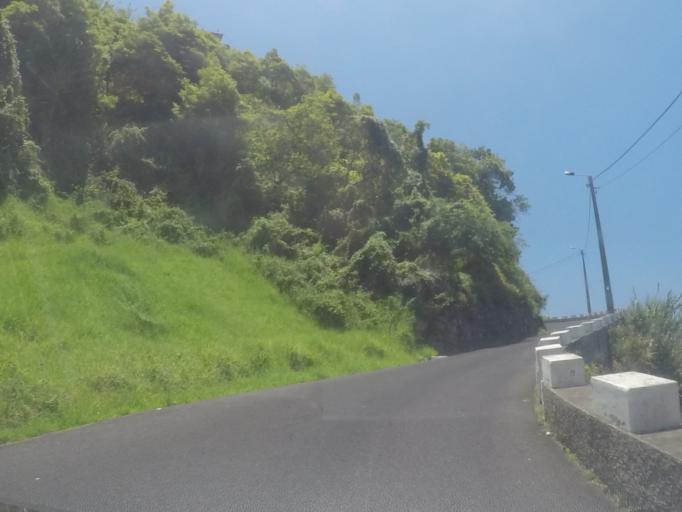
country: PT
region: Madeira
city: Camara de Lobos
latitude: 32.6712
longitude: -16.9843
